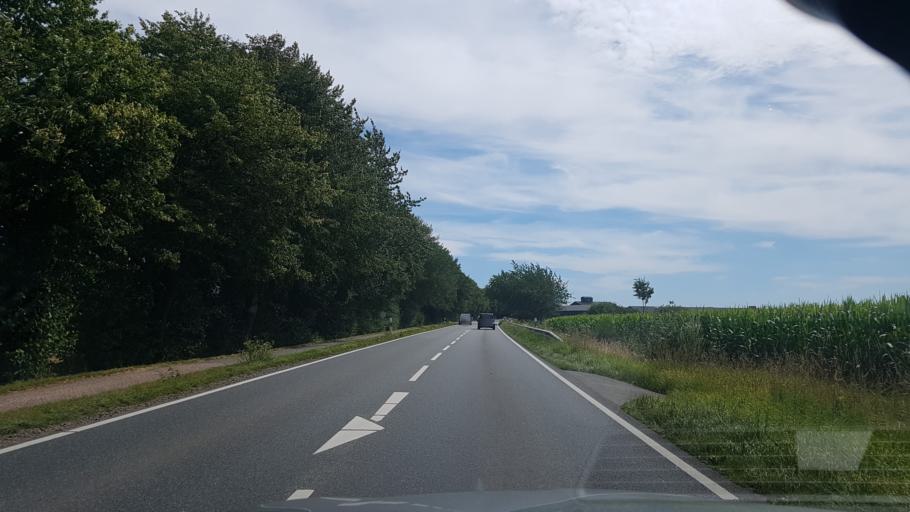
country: DE
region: Schleswig-Holstein
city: Gross Buchwald
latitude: 54.1634
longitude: 10.0969
